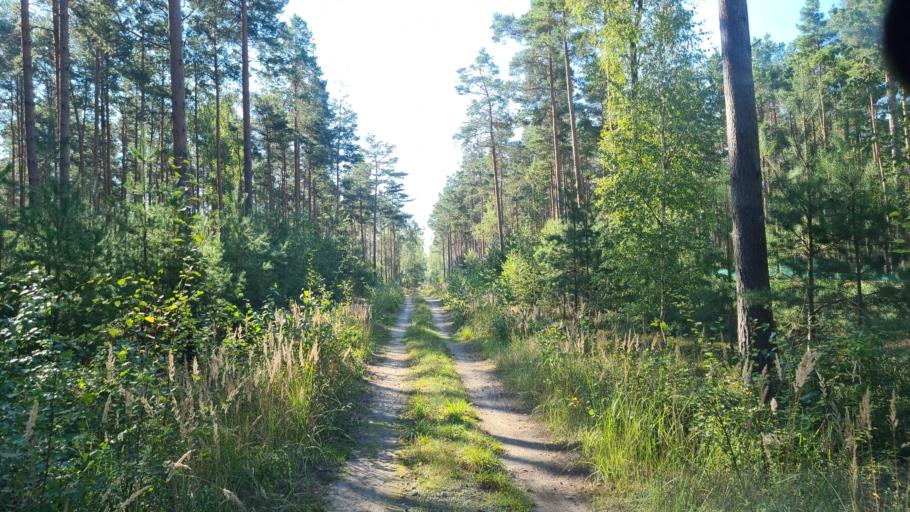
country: DE
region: Brandenburg
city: Schonborn
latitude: 51.6310
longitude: 13.5049
